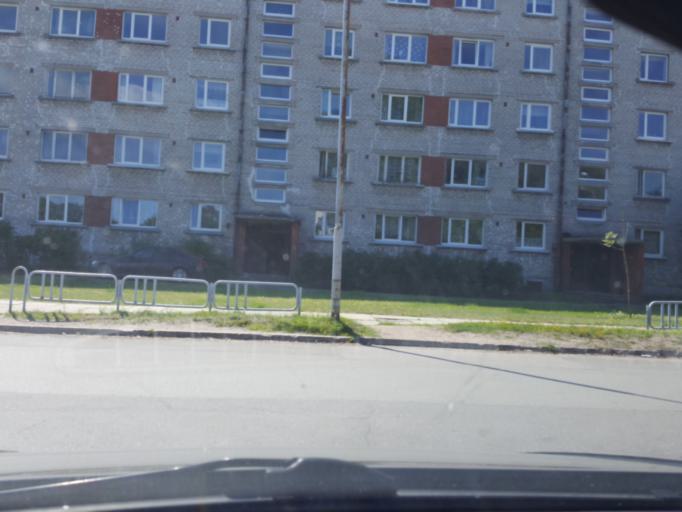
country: LV
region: Liepaja
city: Liepaja
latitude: 56.4912
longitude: 21.0045
